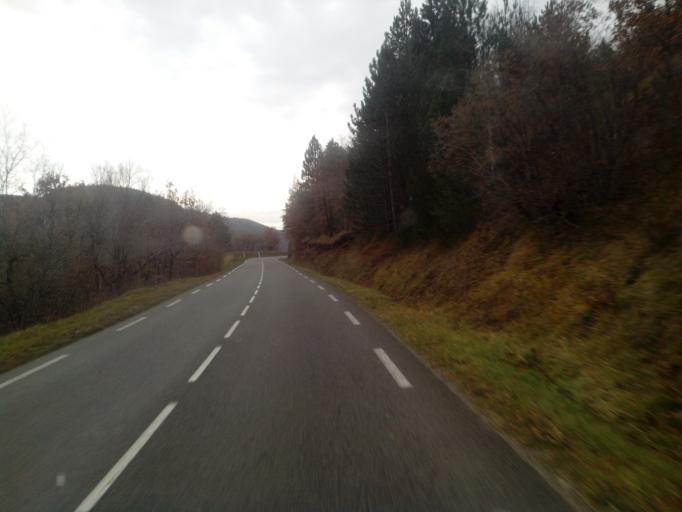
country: FR
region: Languedoc-Roussillon
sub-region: Departement de la Lozere
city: Florac
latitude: 44.2981
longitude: 3.5995
